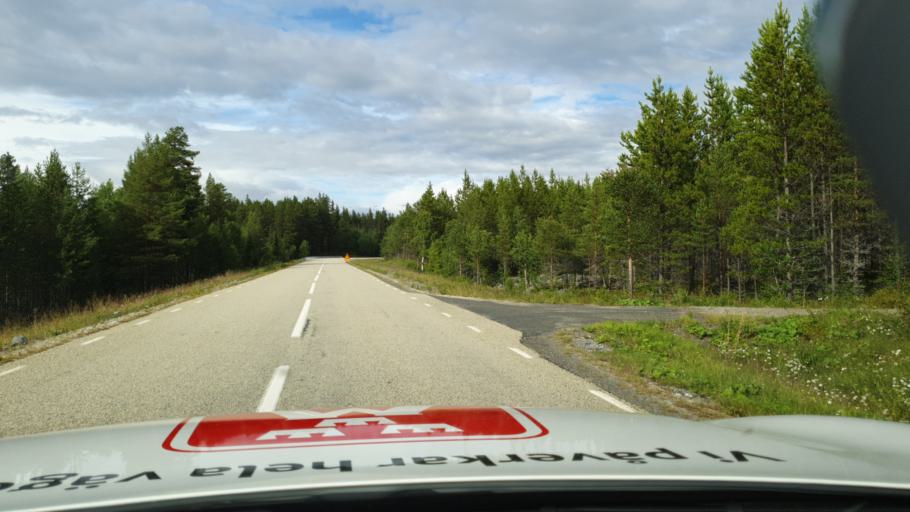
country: SE
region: Jaemtland
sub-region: Are Kommun
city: Are
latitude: 62.8410
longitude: 13.1569
